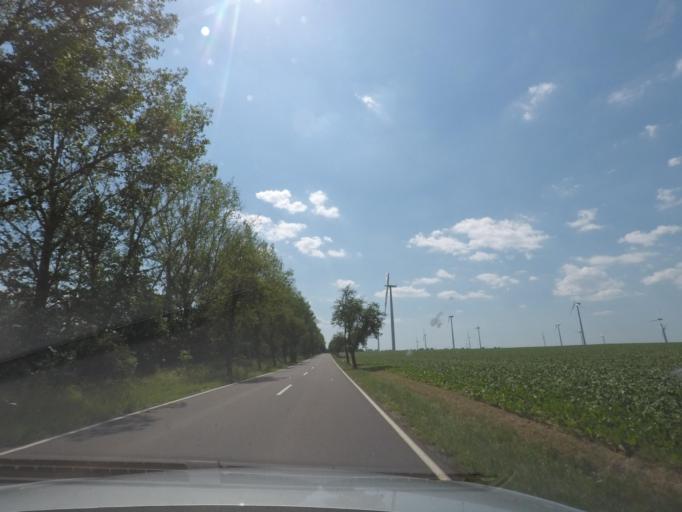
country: DE
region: Saxony-Anhalt
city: Eichenbarleben
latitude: 52.2028
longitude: 11.3864
